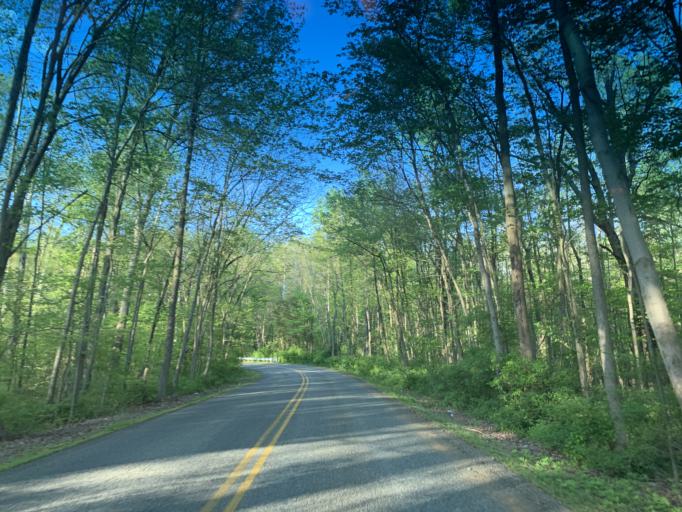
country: US
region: Maryland
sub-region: Harford County
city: Aberdeen
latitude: 39.5349
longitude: -76.1905
